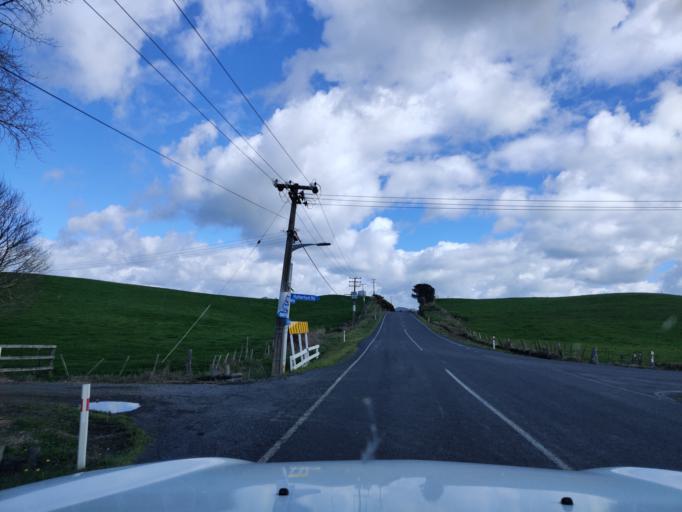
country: NZ
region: Waikato
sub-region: Waikato District
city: Ngaruawahia
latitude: -37.5762
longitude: 175.2360
